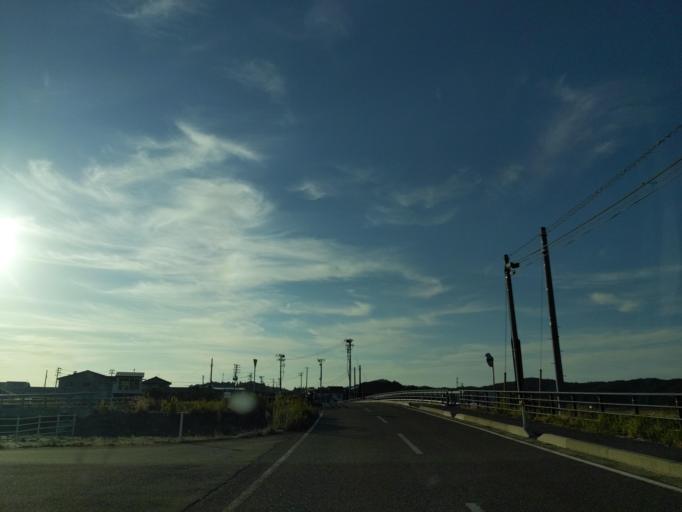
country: JP
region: Niigata
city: Yoshida-kasugacho
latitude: 37.5806
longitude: 138.7780
